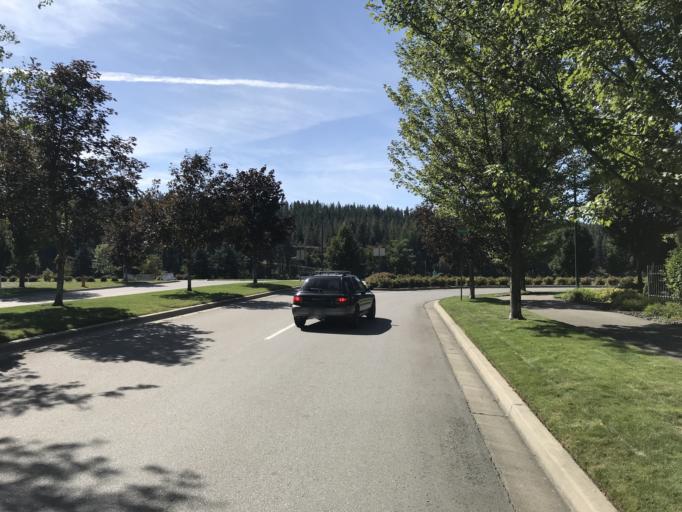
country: US
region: Idaho
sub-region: Kootenai County
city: Coeur d'Alene
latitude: 47.7011
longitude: -116.8403
